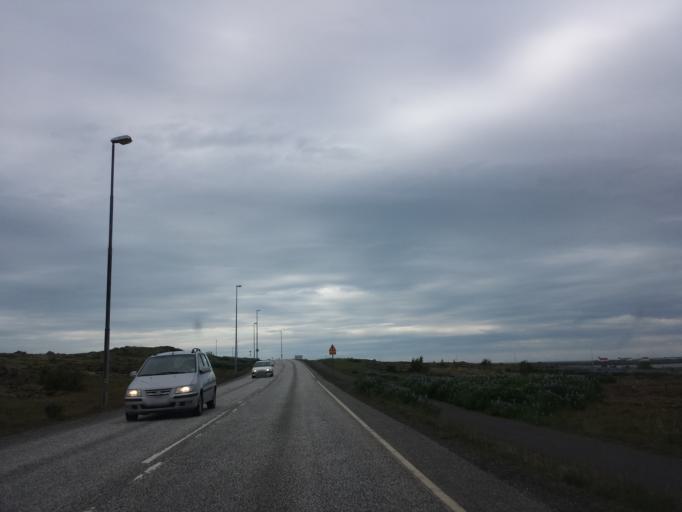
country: IS
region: Capital Region
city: Alftanes
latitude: 64.0879
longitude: -21.9785
